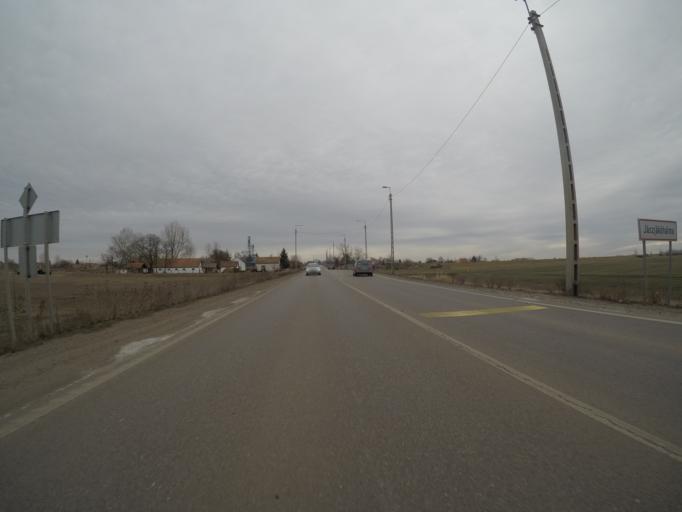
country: HU
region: Jasz-Nagykun-Szolnok
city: Jaszjakohalma
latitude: 47.5191
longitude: 19.9779
